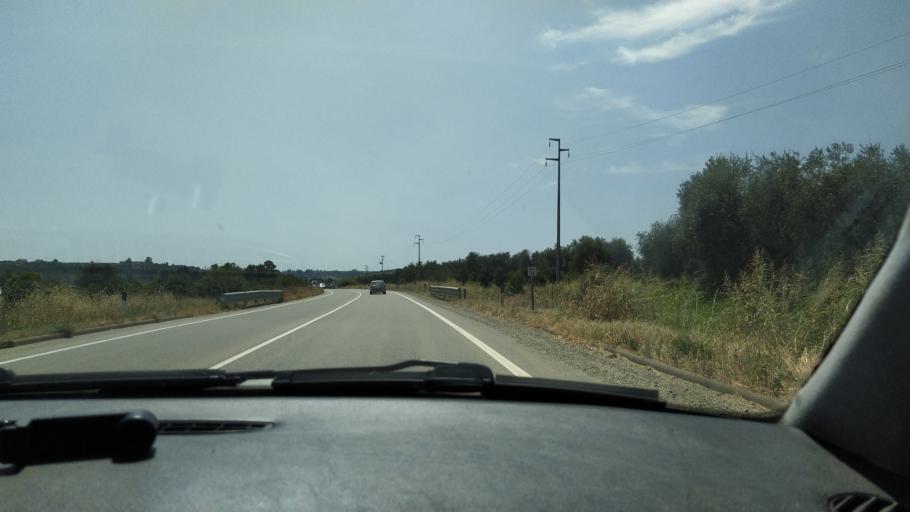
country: IT
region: Basilicate
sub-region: Provincia di Matera
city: Bernalda
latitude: 40.4490
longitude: 16.7760
